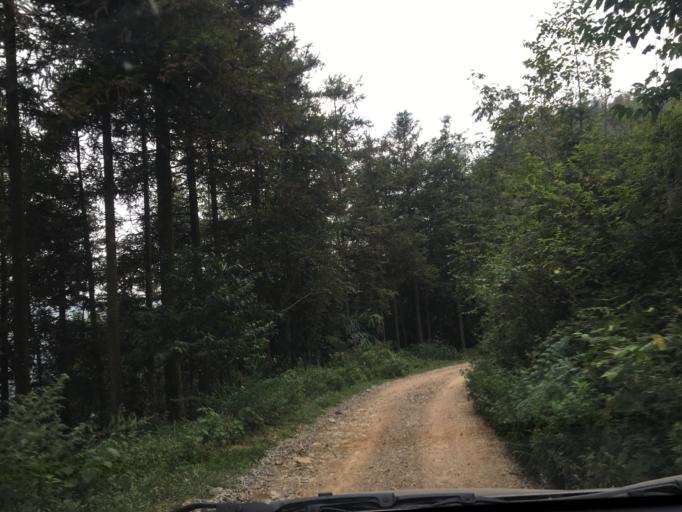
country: CN
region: Guangxi Zhuangzu Zizhiqu
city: Xinzhou
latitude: 25.5396
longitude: 105.5293
